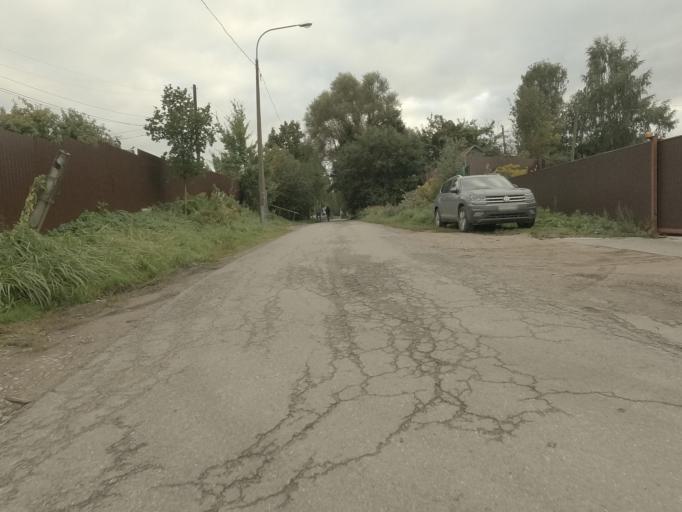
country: RU
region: St.-Petersburg
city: Krasnogvargeisky
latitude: 59.9746
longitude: 30.5139
